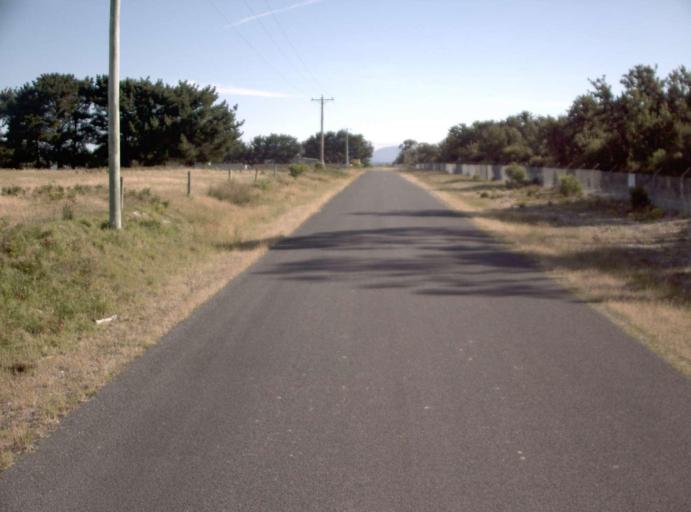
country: AU
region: Victoria
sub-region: Latrobe
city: Morwell
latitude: -38.7120
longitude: 146.3964
